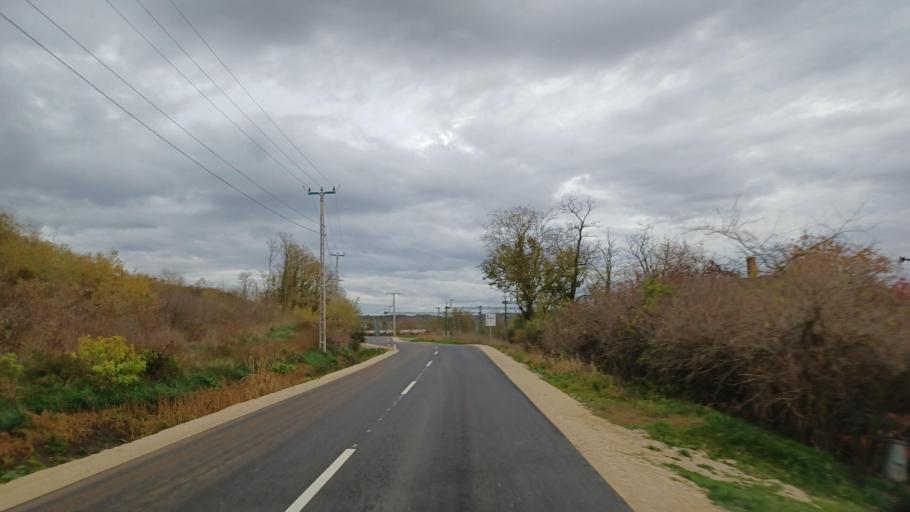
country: HU
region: Tolna
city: Gyonk
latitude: 46.6009
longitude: 18.4245
